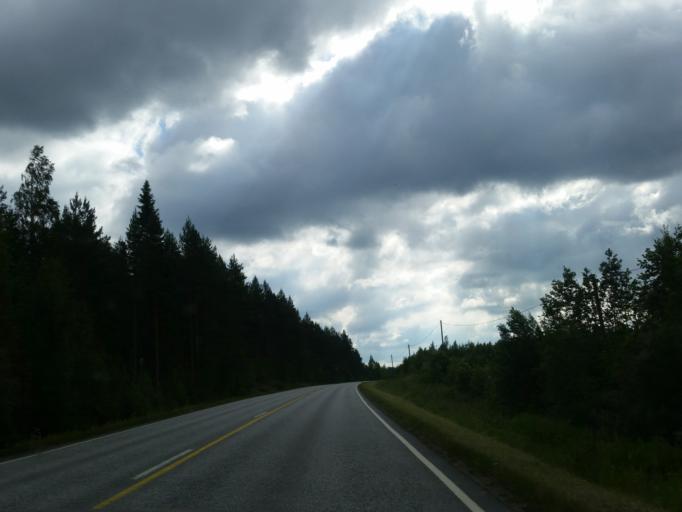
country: FI
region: Northern Savo
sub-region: Sisae-Savo
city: Suonenjoki
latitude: 62.8579
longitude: 27.2381
